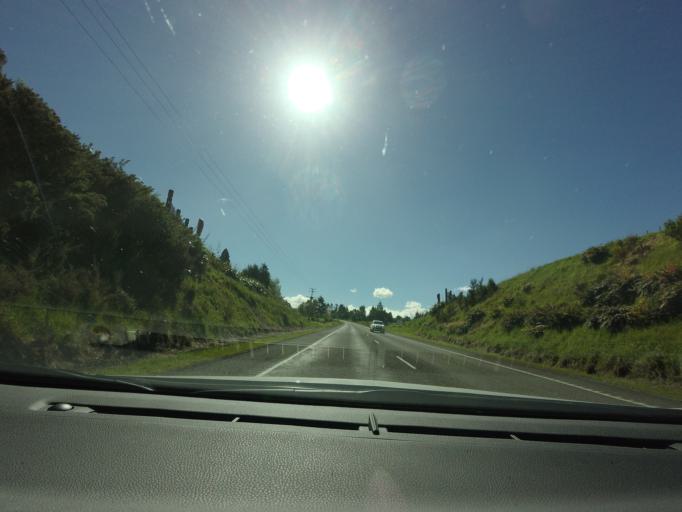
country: NZ
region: Bay of Plenty
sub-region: Rotorua District
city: Rotorua
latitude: -38.0730
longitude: 176.1522
